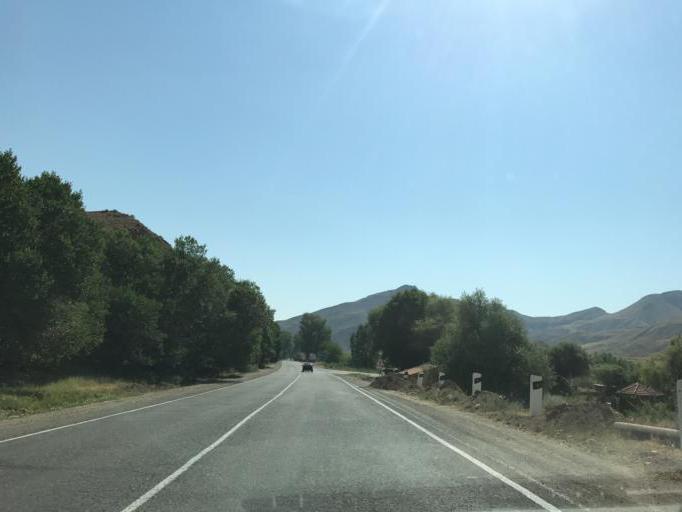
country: AM
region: Vayots' Dzori Marz
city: Getap'
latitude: 39.7360
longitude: 45.2870
